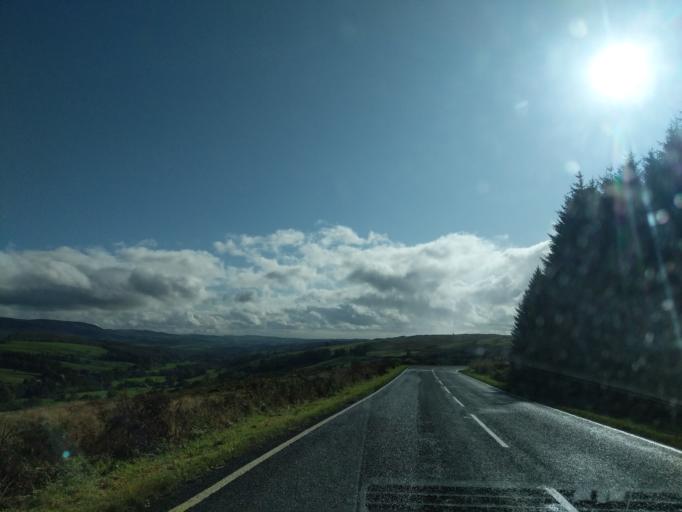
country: GB
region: Scotland
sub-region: Dumfries and Galloway
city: Moffat
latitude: 55.3680
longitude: -3.4746
